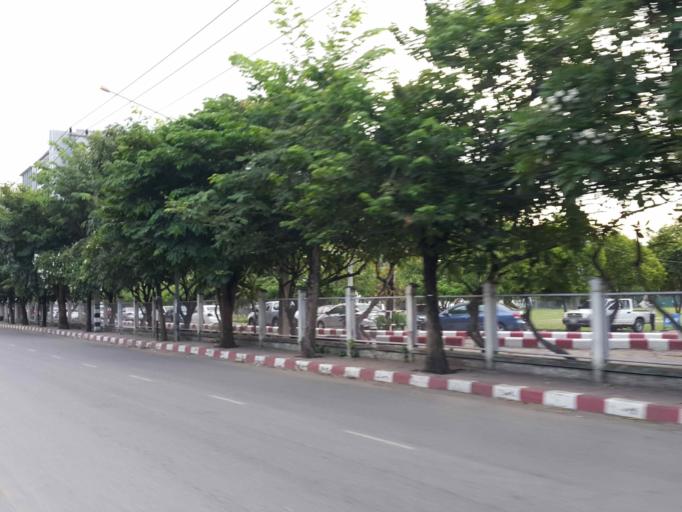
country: TH
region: Chiang Mai
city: Chiang Mai
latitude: 18.7891
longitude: 98.9721
